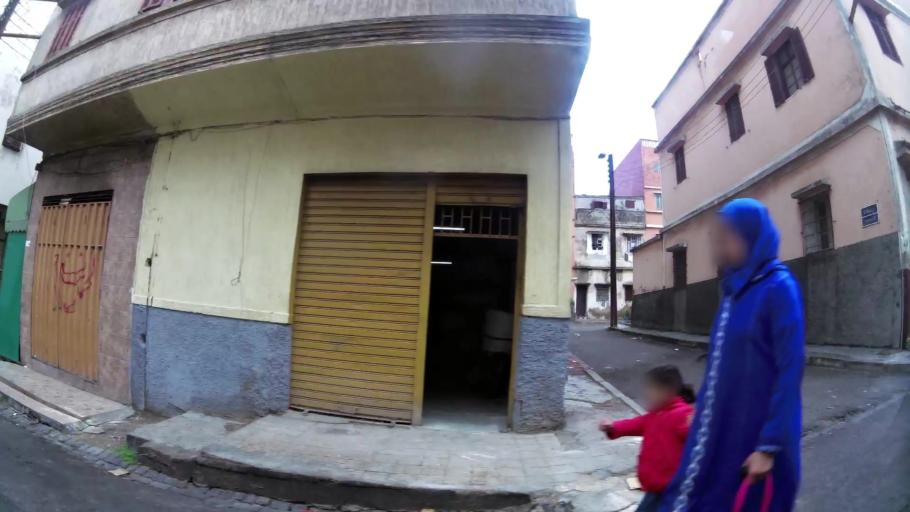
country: MA
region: Grand Casablanca
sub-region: Casablanca
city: Casablanca
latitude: 33.5546
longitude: -7.6041
